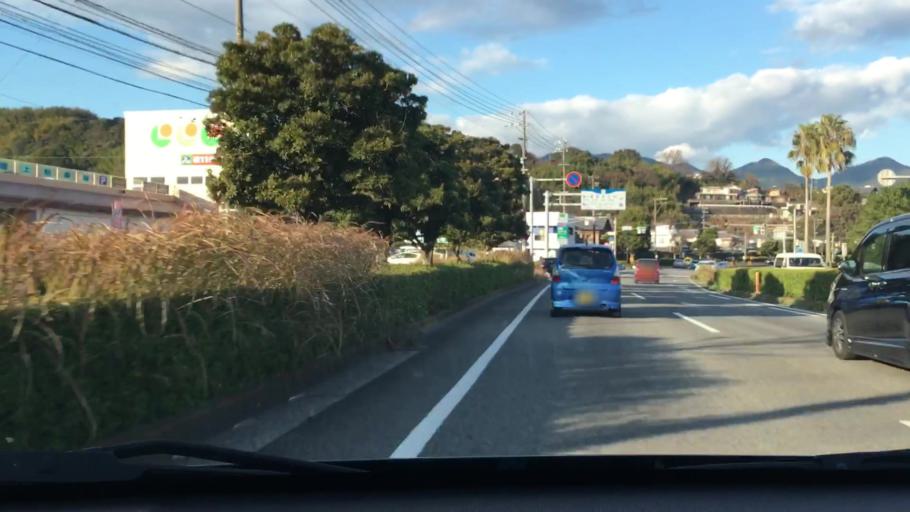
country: JP
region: Oita
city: Hiji
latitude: 33.3431
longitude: 131.4944
